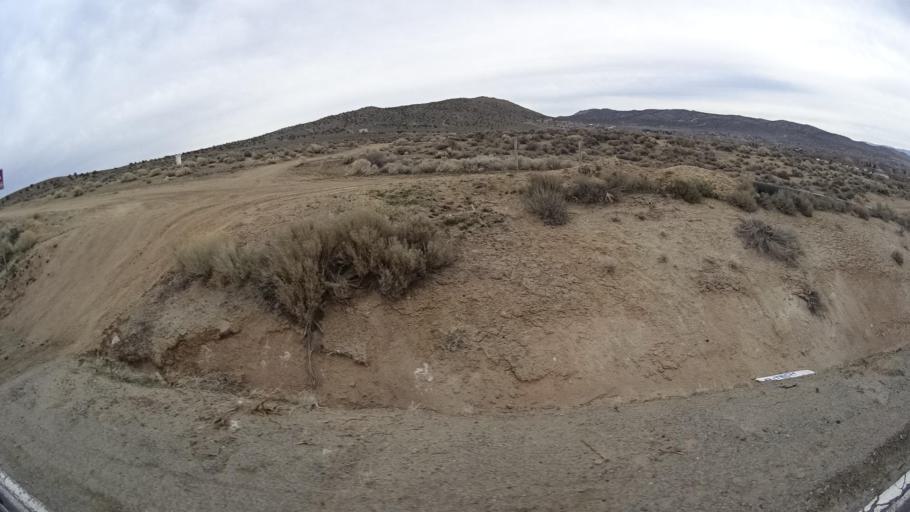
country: US
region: Nevada
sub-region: Washoe County
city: Lemmon Valley
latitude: 39.6766
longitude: -119.8539
